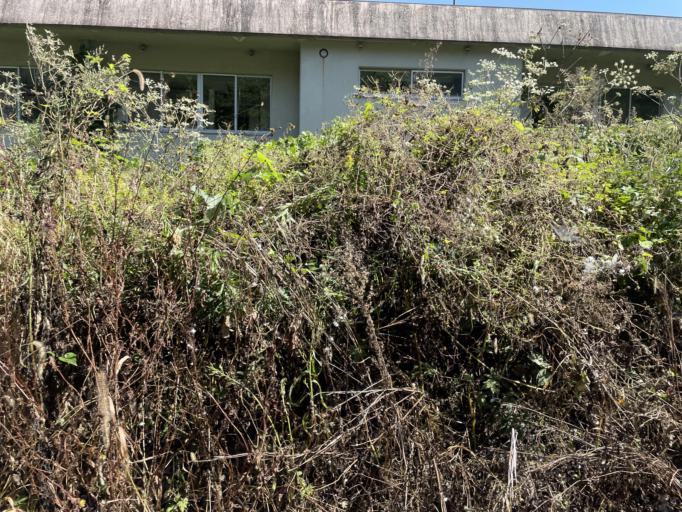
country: JP
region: Nara
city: Yoshino-cho
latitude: 34.3878
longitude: 135.8492
